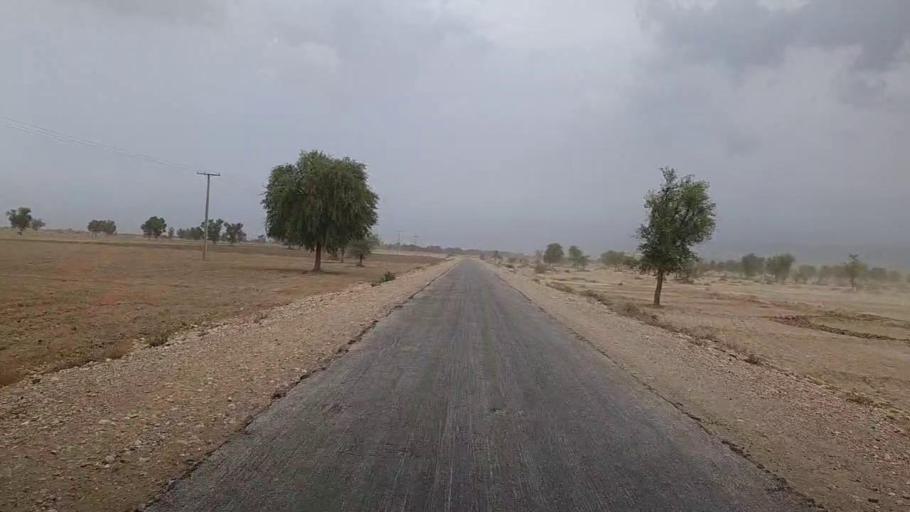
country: PK
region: Sindh
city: Sehwan
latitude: 26.3140
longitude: 67.7302
